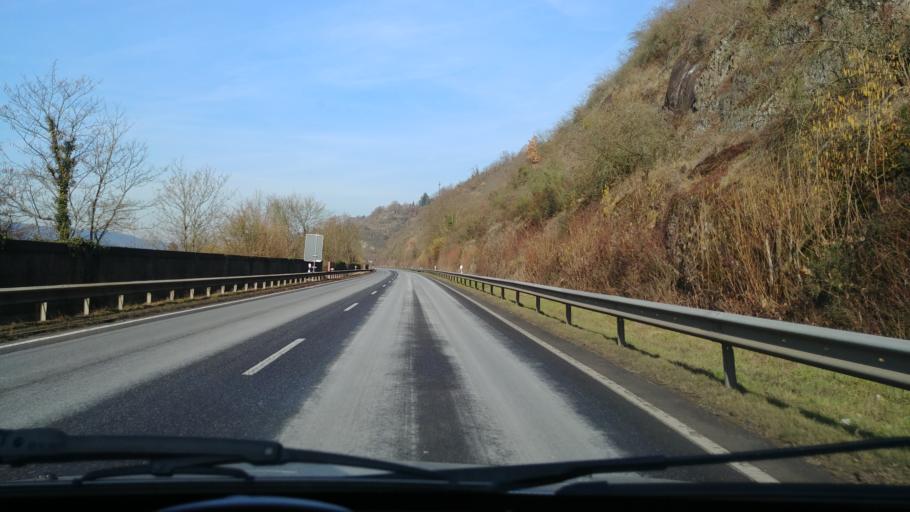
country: DE
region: Rheinland-Pfalz
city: Lahnstein
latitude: 50.2923
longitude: 7.6229
